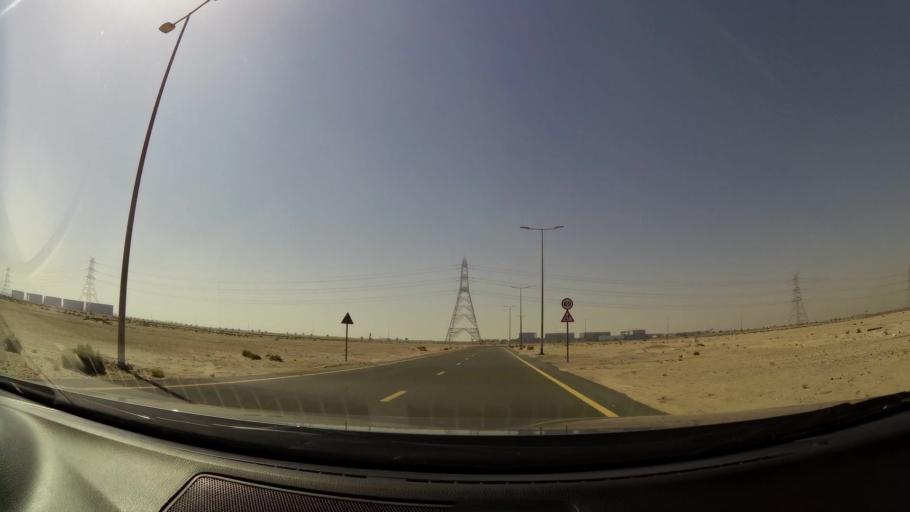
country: AE
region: Dubai
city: Dubai
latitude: 24.9031
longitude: 55.0656
